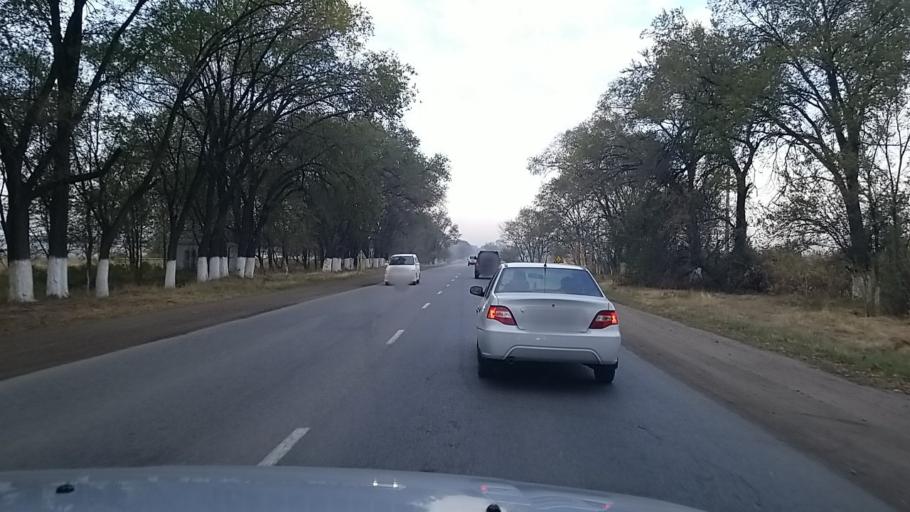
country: KZ
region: Almaty Oblysy
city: Burunday
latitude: 43.3583
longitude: 76.7748
